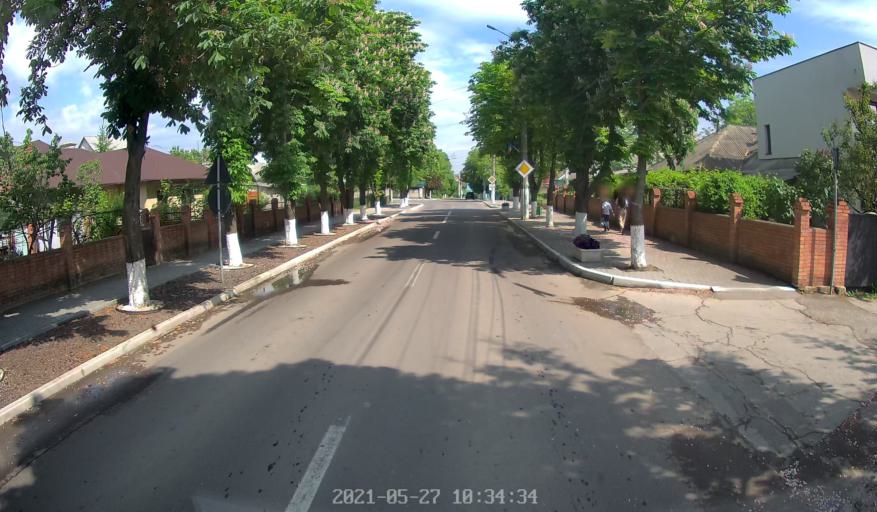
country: MD
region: Chisinau
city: Stauceni
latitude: 47.0903
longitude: 28.8682
